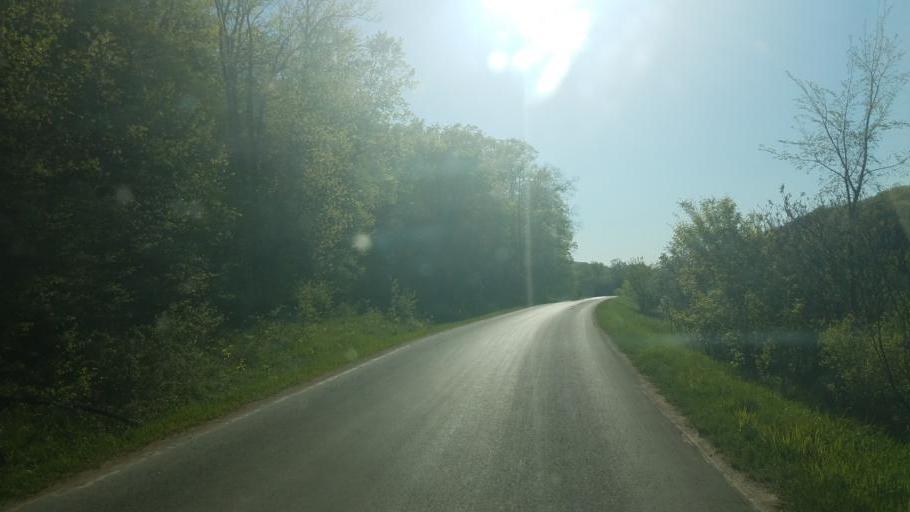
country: US
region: Wisconsin
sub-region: Vernon County
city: Hillsboro
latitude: 43.6244
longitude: -90.4776
